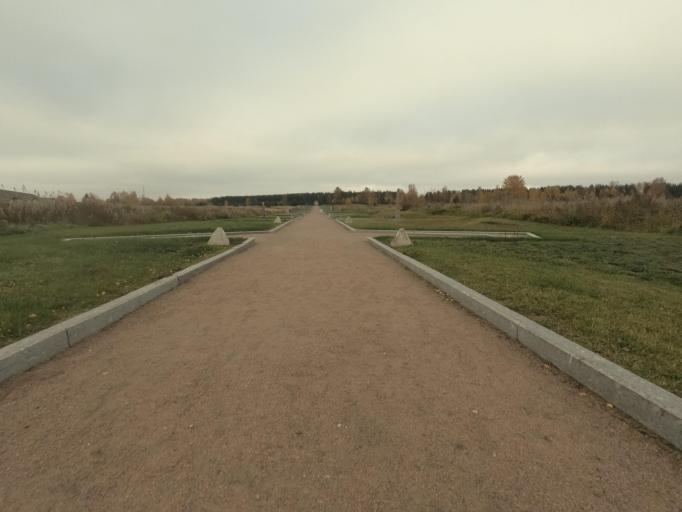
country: RU
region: Leningrad
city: Kirovsk
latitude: 59.8463
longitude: 30.9497
